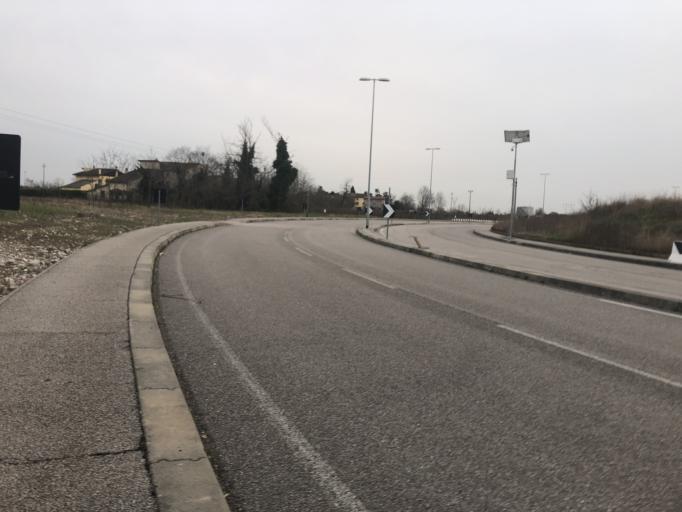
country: IT
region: Veneto
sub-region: Provincia di Verona
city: Dossobuono
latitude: 45.4143
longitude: 10.9338
